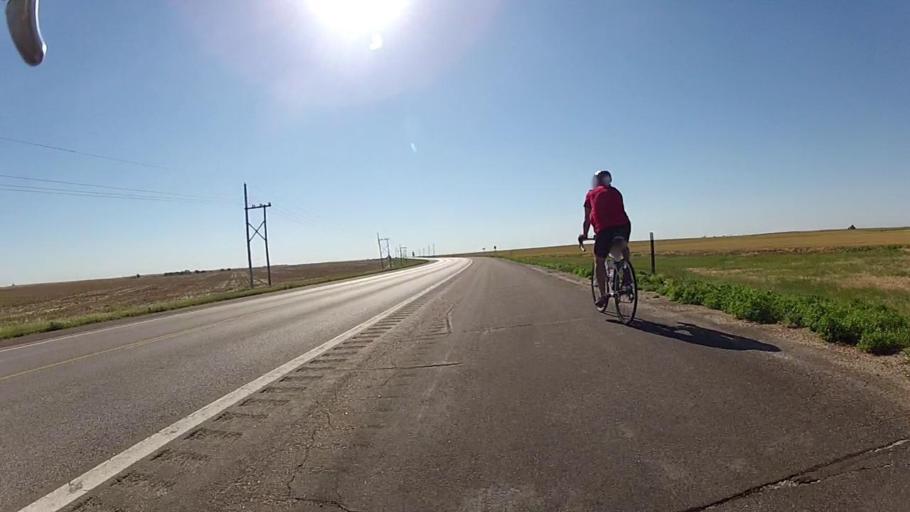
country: US
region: Kansas
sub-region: Ford County
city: Dodge City
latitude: 37.5866
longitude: -99.6809
